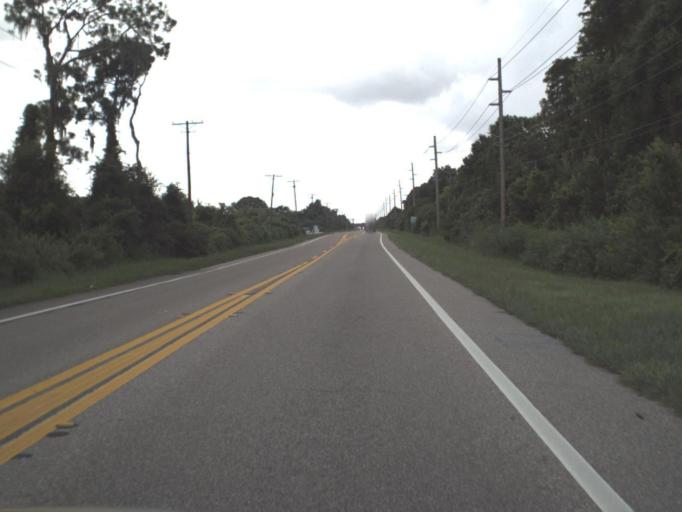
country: US
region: Florida
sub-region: Hillsborough County
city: Sun City Center
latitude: 27.7325
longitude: -82.3352
